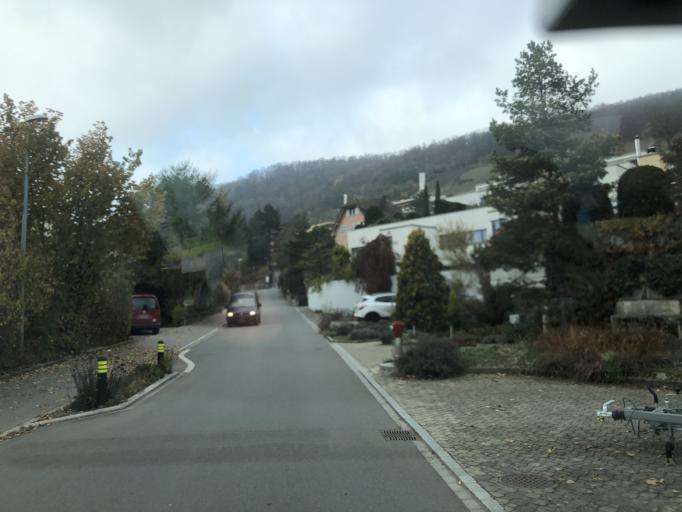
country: CH
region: Aargau
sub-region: Bezirk Baden
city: Wettingen
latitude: 47.4696
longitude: 8.3300
